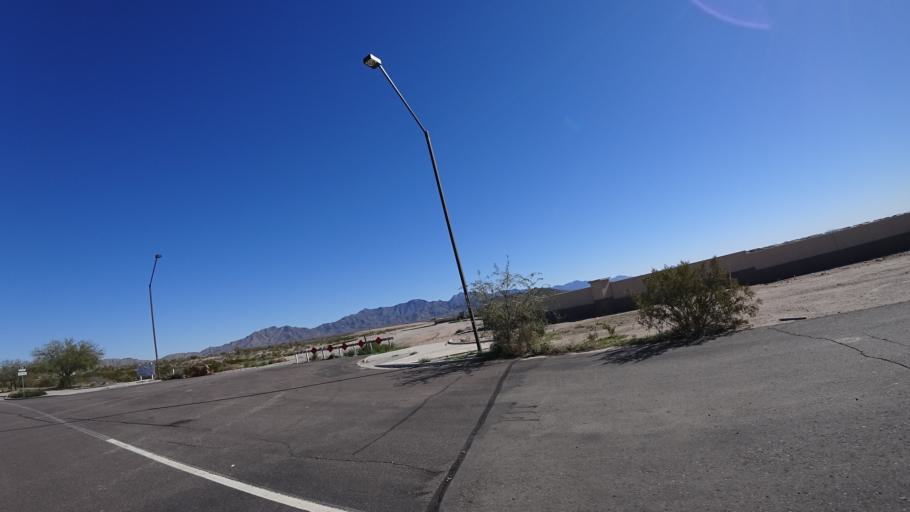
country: US
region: Arizona
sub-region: Maricopa County
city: Goodyear
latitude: 33.3011
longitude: -112.4403
